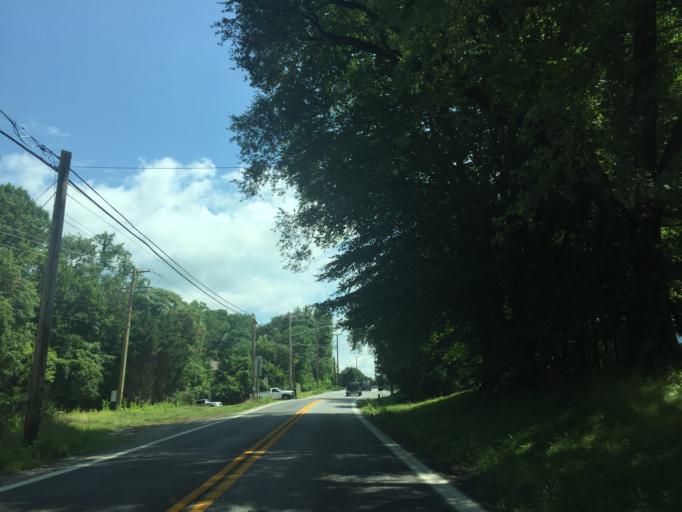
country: US
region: Maryland
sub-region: Baltimore County
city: Kingsville
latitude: 39.4603
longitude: -76.4574
